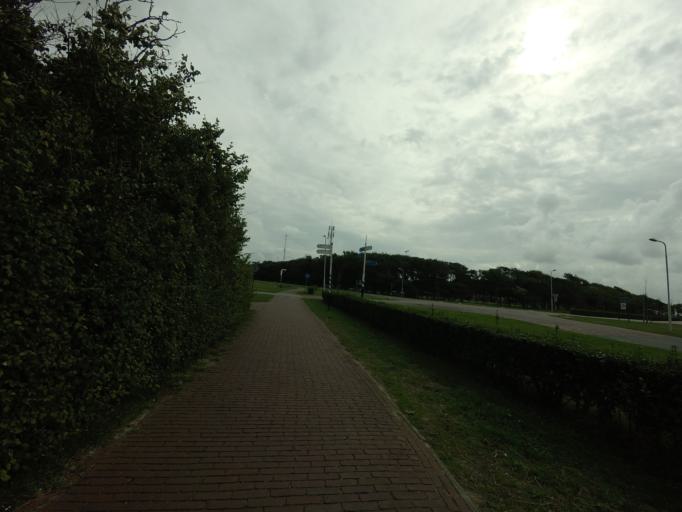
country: NL
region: Friesland
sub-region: Gemeente Ameland
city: Hollum
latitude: 53.4462
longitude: 5.6347
